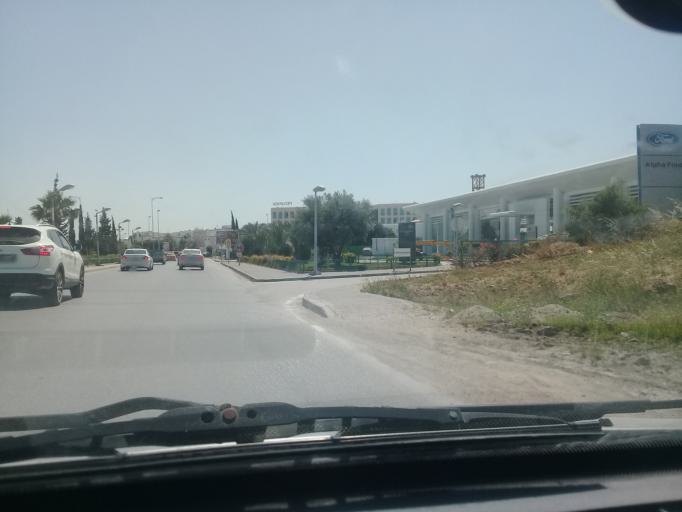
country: TN
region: Ariana
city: Ariana
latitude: 36.8418
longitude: 10.2488
